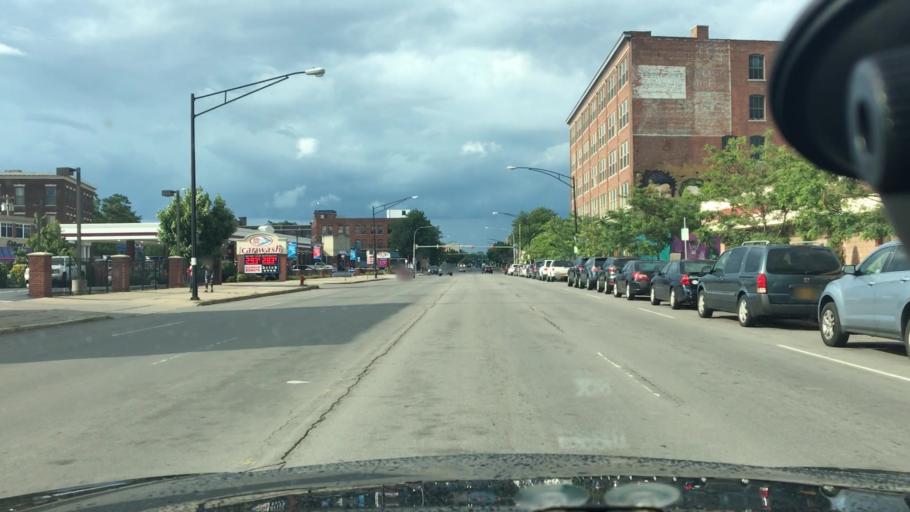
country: US
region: New York
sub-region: Erie County
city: Buffalo
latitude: 42.9061
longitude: -78.8677
